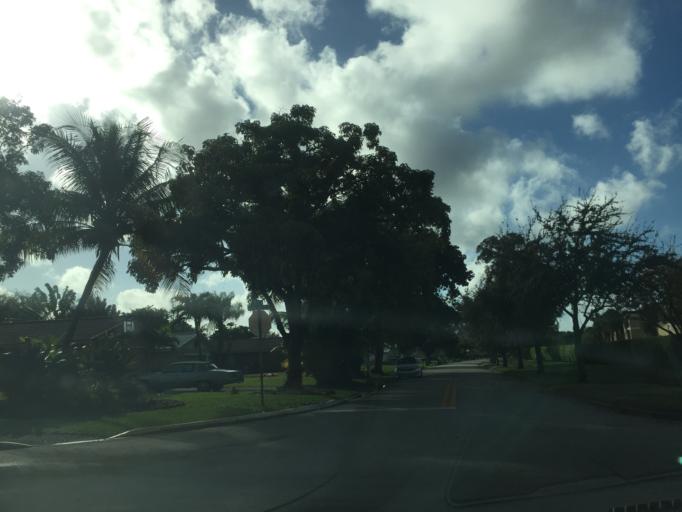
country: US
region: Florida
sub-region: Broward County
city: North Lauderdale
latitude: 26.2433
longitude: -80.2414
